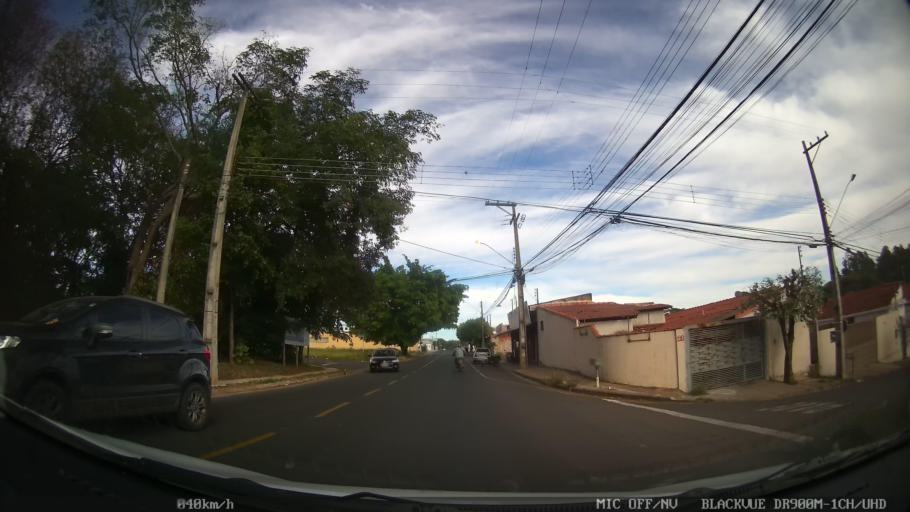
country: BR
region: Sao Paulo
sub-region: Catanduva
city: Catanduva
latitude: -21.1399
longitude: -49.0006
